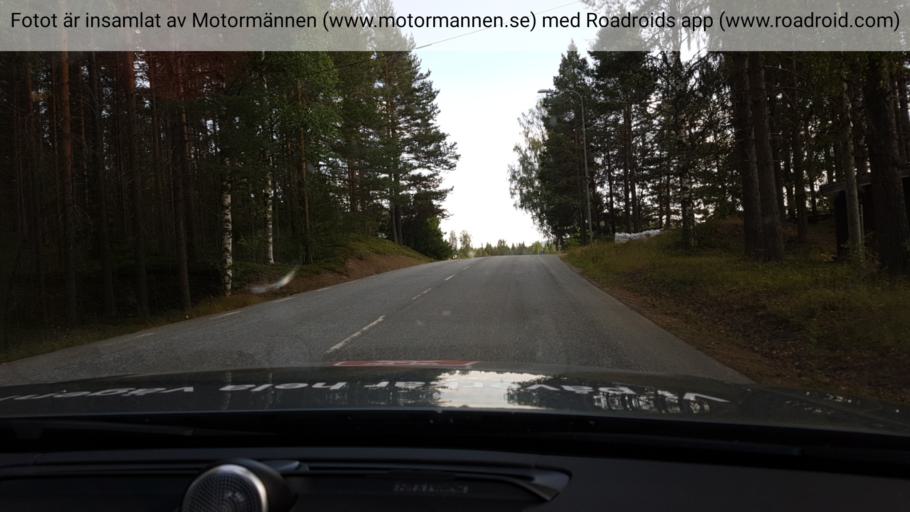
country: SE
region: Vaesterbotten
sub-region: Dorotea Kommun
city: Dorotea
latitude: 63.9202
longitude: 16.3423
